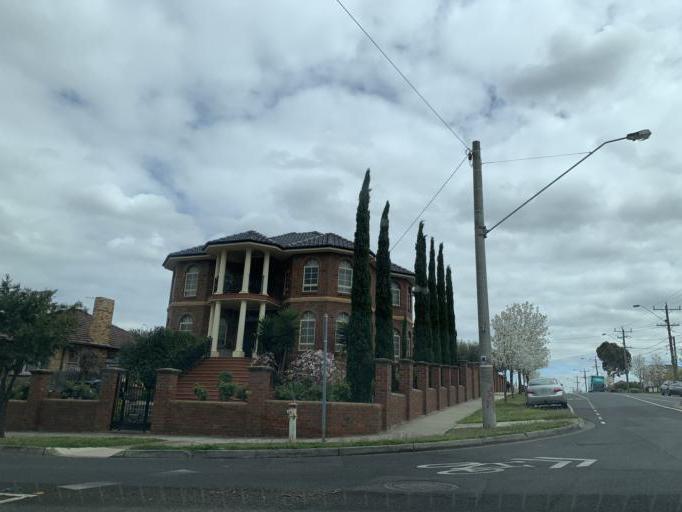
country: AU
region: Victoria
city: Thornbury
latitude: -37.7396
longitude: 144.9948
